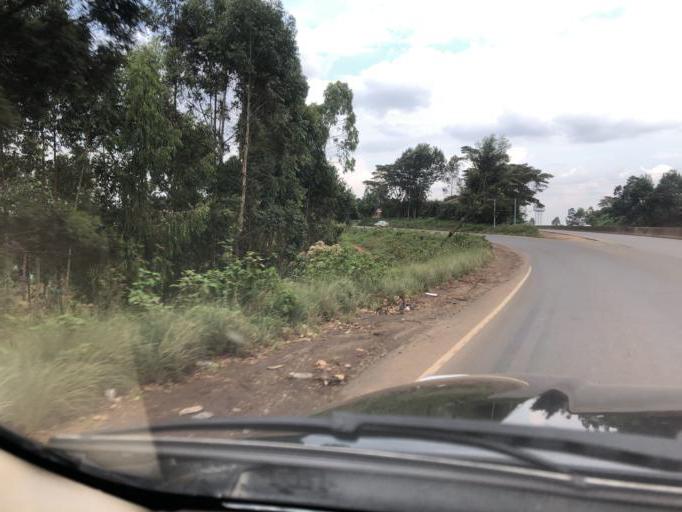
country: KE
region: Kiambu
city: Kikuyu
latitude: -1.2279
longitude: 36.6647
